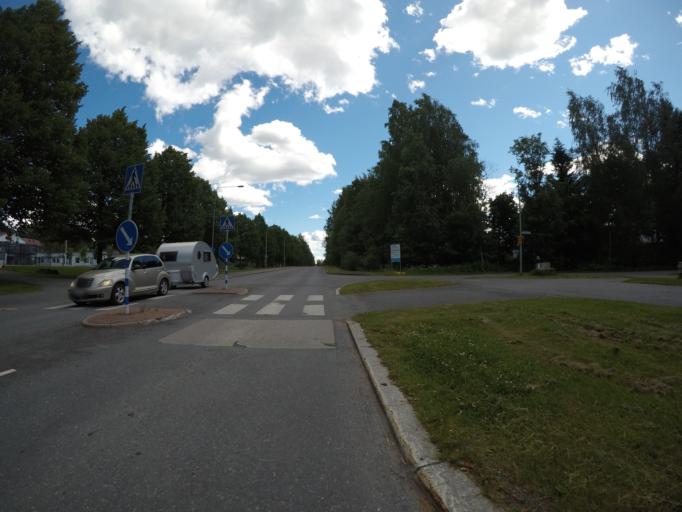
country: FI
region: Haeme
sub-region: Haemeenlinna
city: Haemeenlinna
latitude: 61.0105
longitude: 24.4378
